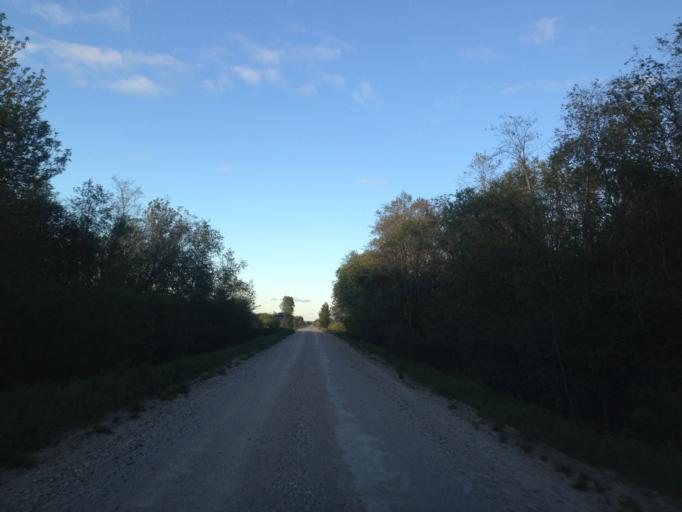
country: EE
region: Raplamaa
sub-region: Maerjamaa vald
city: Marjamaa
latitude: 58.7387
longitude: 24.1638
